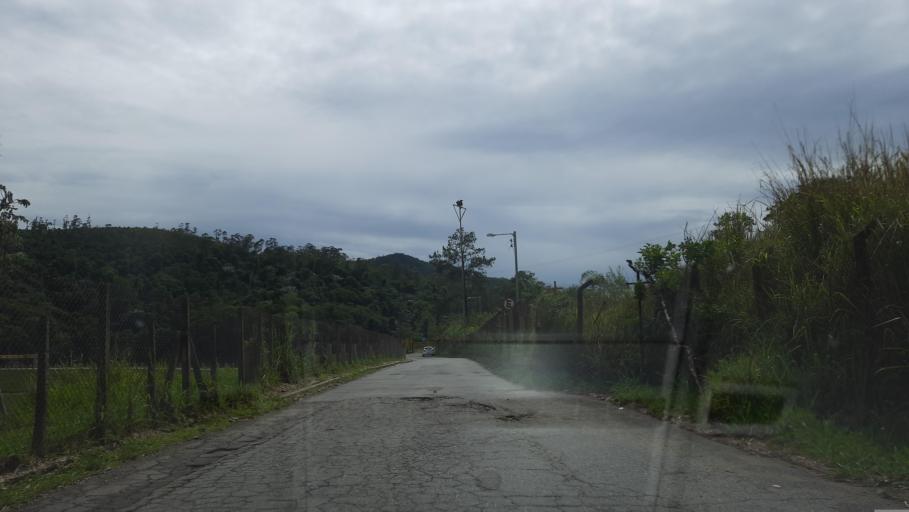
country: BR
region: Sao Paulo
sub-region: Franco Da Rocha
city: Franco da Rocha
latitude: -23.3315
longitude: -46.6807
